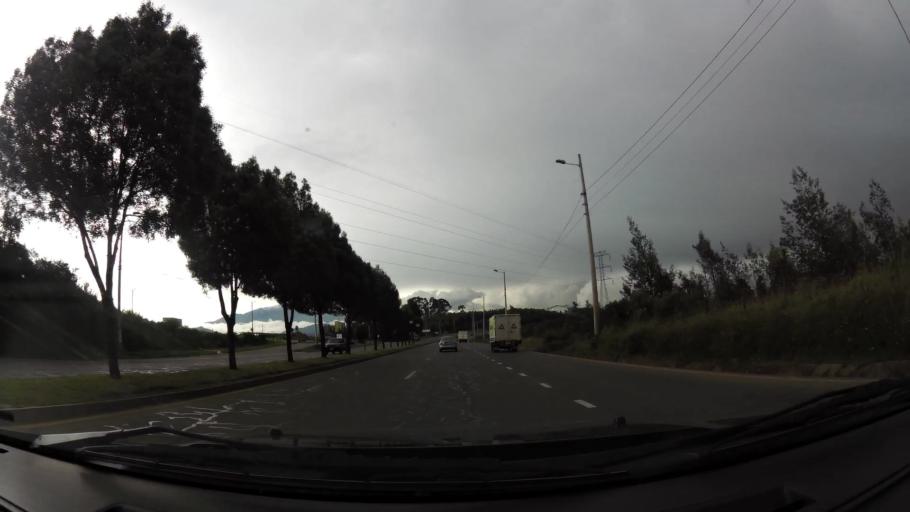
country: EC
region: Pichincha
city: Sangolqui
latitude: -0.3147
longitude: -78.5220
